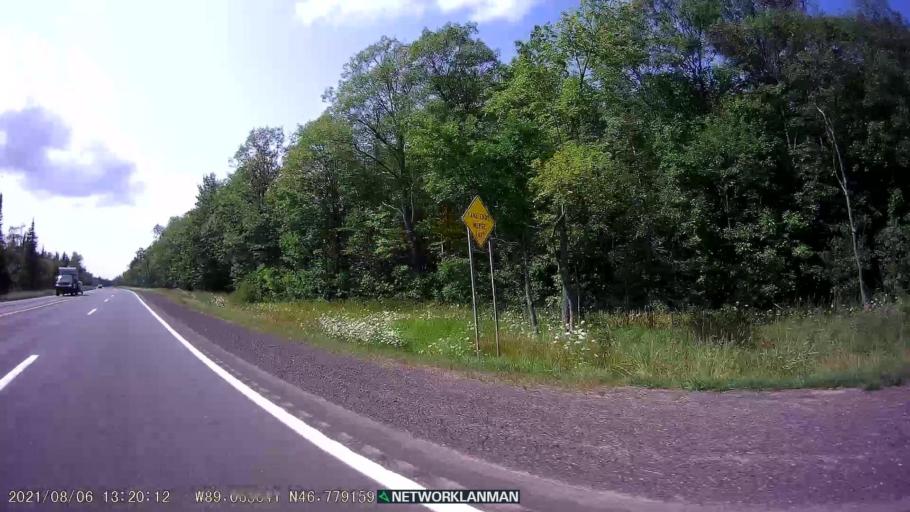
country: US
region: Michigan
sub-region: Ontonagon County
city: Ontonagon
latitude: 46.7793
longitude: -89.0667
